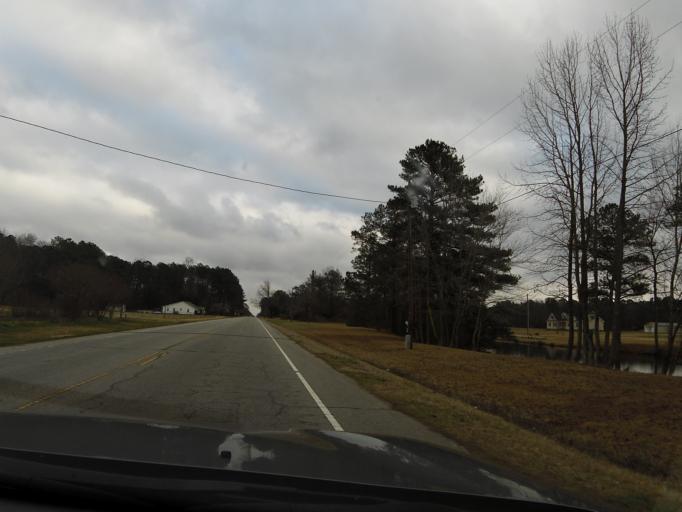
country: US
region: North Carolina
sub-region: Nash County
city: Rocky Mount
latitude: 35.8638
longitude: -77.7151
